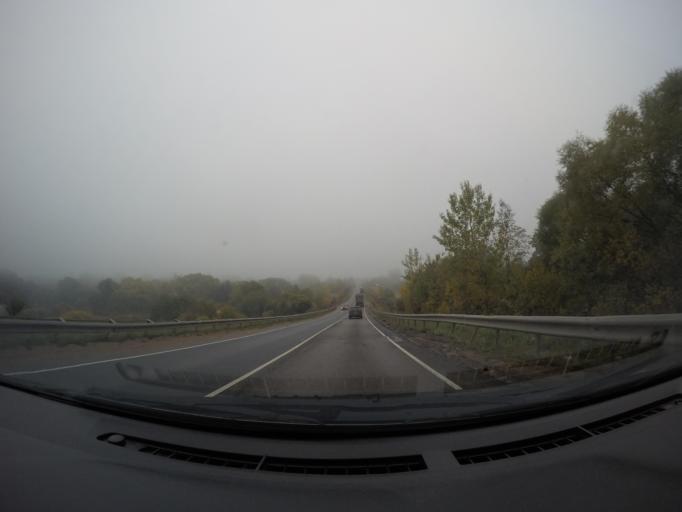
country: RU
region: Moskovskaya
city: Kostrovo
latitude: 55.8677
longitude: 36.6060
